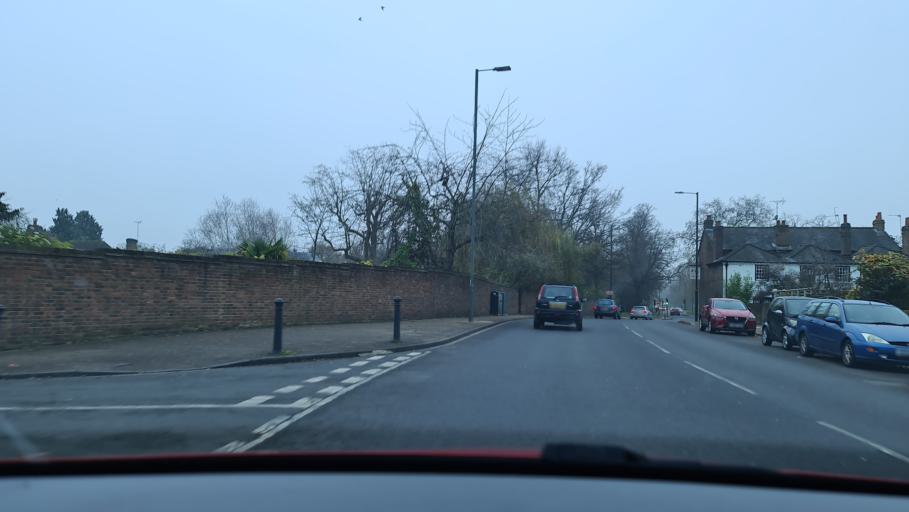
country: GB
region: England
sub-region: Greater London
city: Richmond
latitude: 51.4368
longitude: -0.3046
